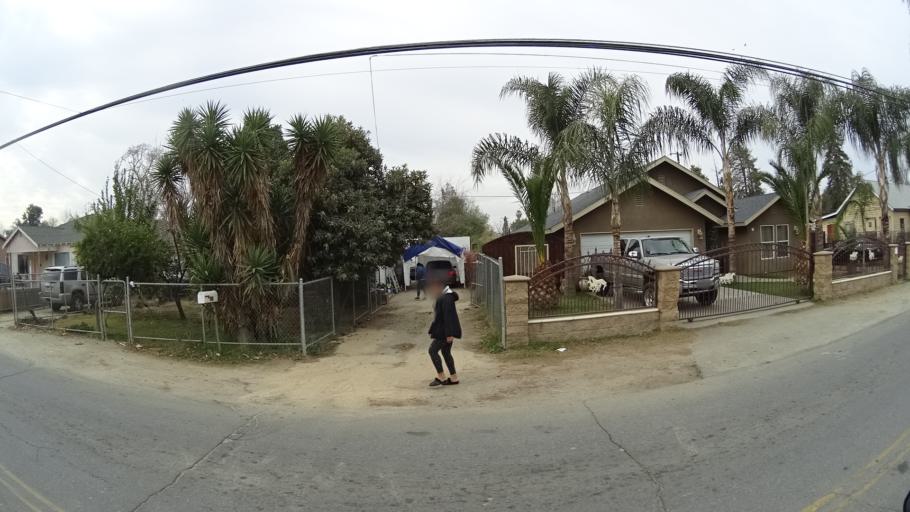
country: US
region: California
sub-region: Kern County
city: Bakersfield
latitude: 35.3427
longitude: -118.9942
